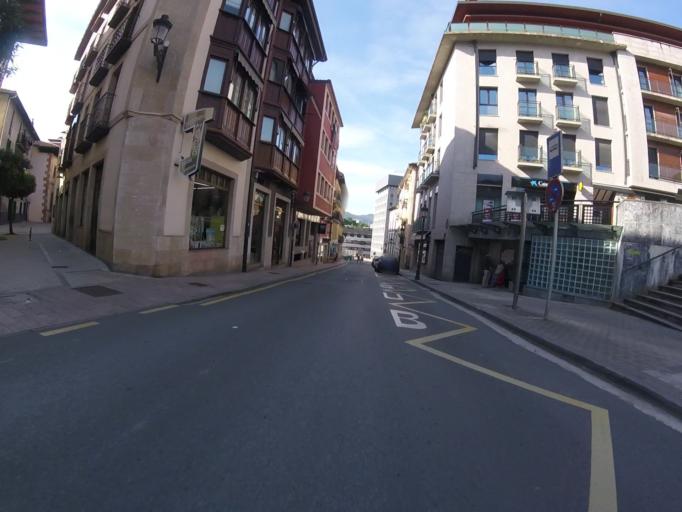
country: ES
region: Basque Country
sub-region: Provincia de Guipuzcoa
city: Villafranca de Ordizia
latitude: 43.0541
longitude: -2.1802
